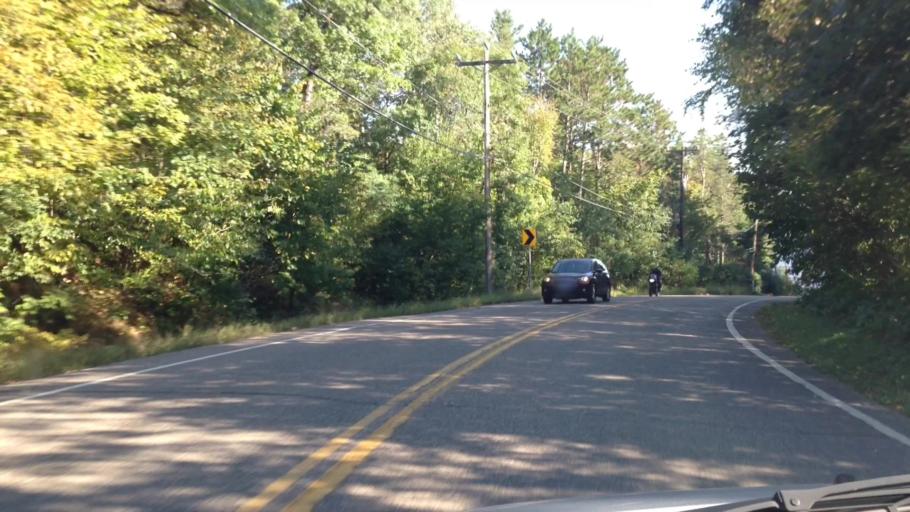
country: US
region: Minnesota
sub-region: Washington County
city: Stillwater
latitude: 45.0805
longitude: -92.8066
